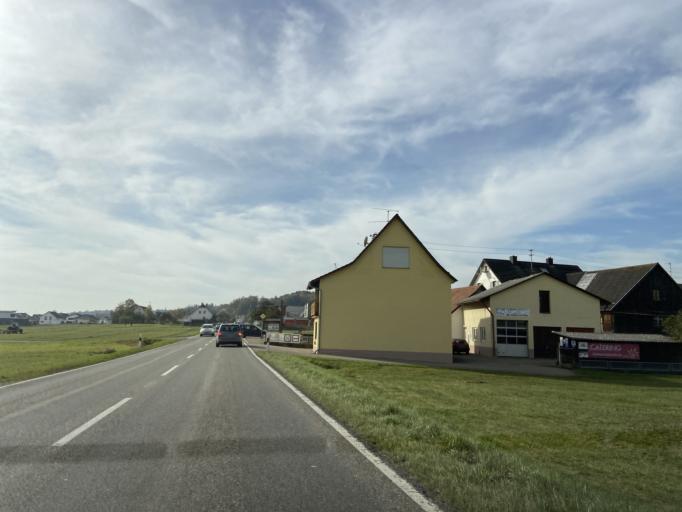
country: DE
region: Baden-Wuerttemberg
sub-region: Tuebingen Region
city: Inzigkofen
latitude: 48.0618
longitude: 9.1484
